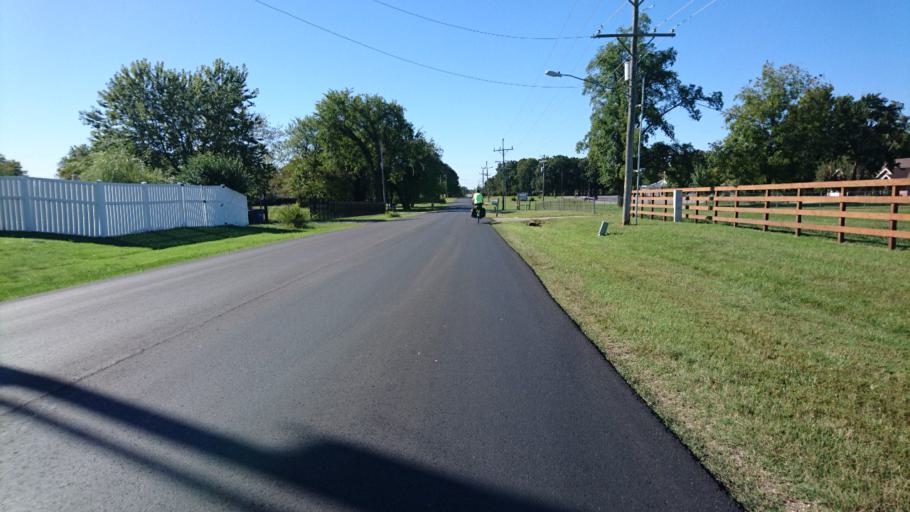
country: US
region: Missouri
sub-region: Jasper County
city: Joplin
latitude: 37.1191
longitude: -94.4938
